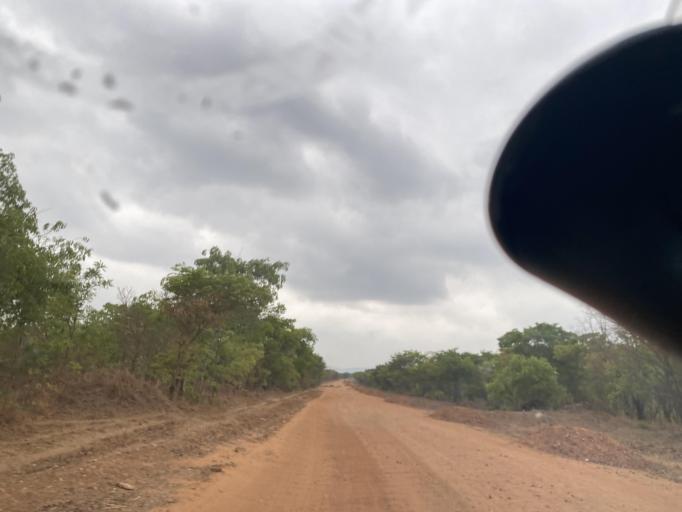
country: ZM
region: Lusaka
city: Chongwe
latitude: -15.2681
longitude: 28.7318
